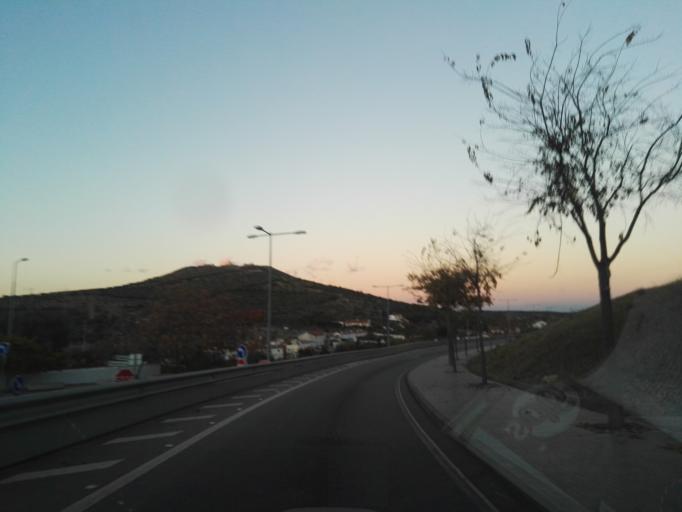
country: PT
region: Portalegre
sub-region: Elvas
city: Elvas
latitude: 38.8828
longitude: -7.1706
